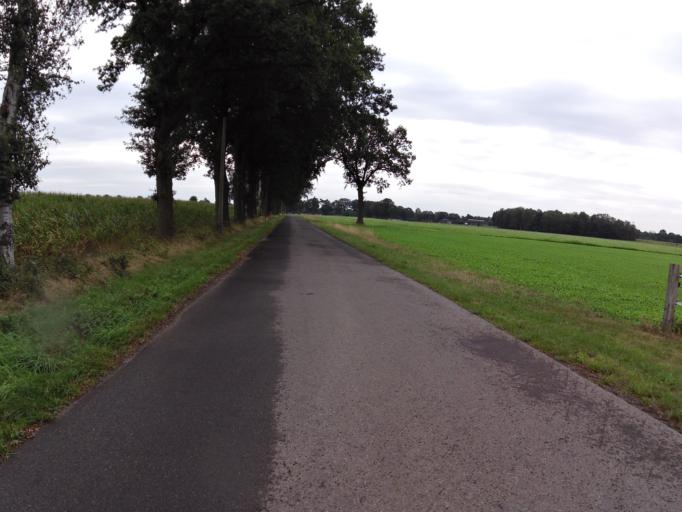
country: DE
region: Lower Saxony
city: Helvesiek
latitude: 53.2145
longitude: 9.4598
